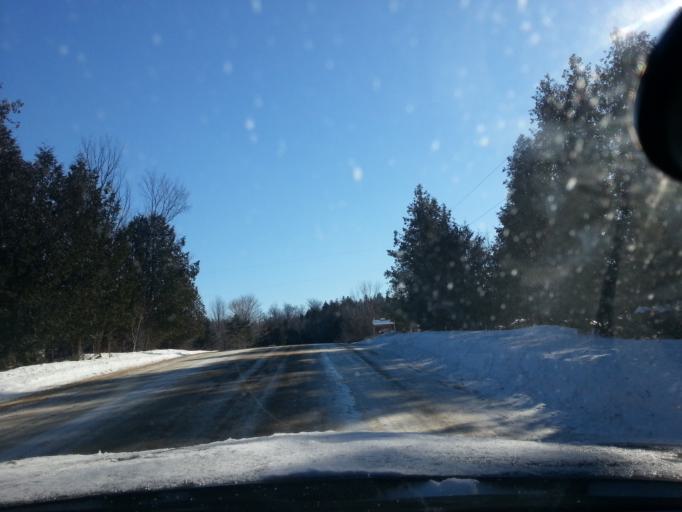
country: CA
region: Ontario
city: Arnprior
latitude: 45.2490
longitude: -76.3096
